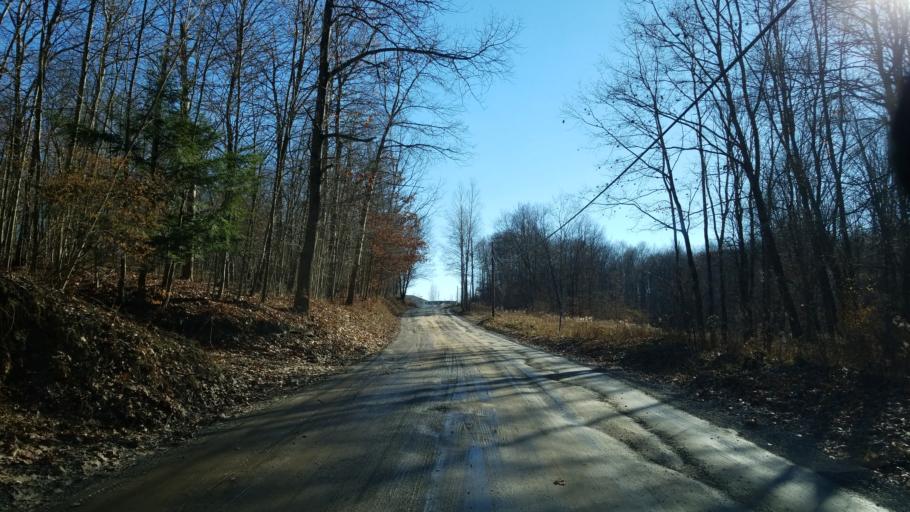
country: US
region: Pennsylvania
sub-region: Jefferson County
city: Falls Creek
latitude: 41.1309
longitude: -78.7885
